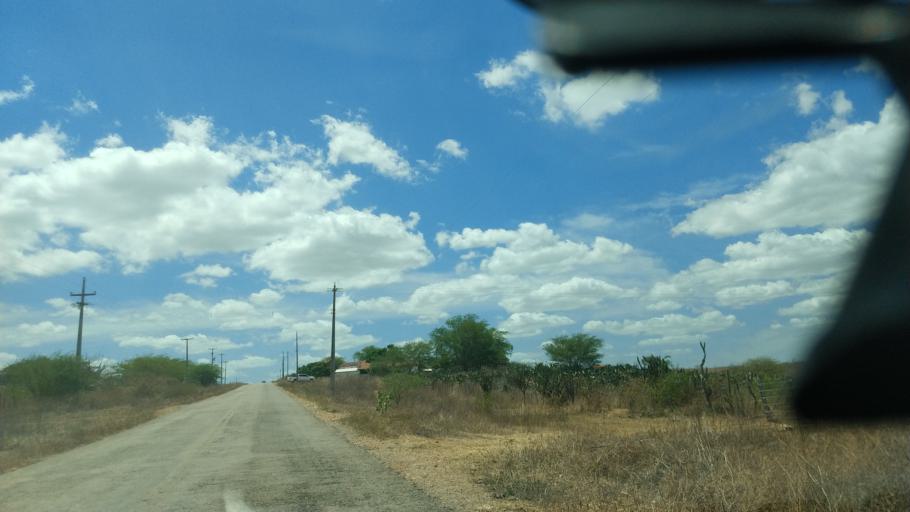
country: BR
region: Rio Grande do Norte
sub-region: Sao Paulo Do Potengi
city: Sao Paulo do Potengi
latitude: -5.9664
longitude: -35.8901
